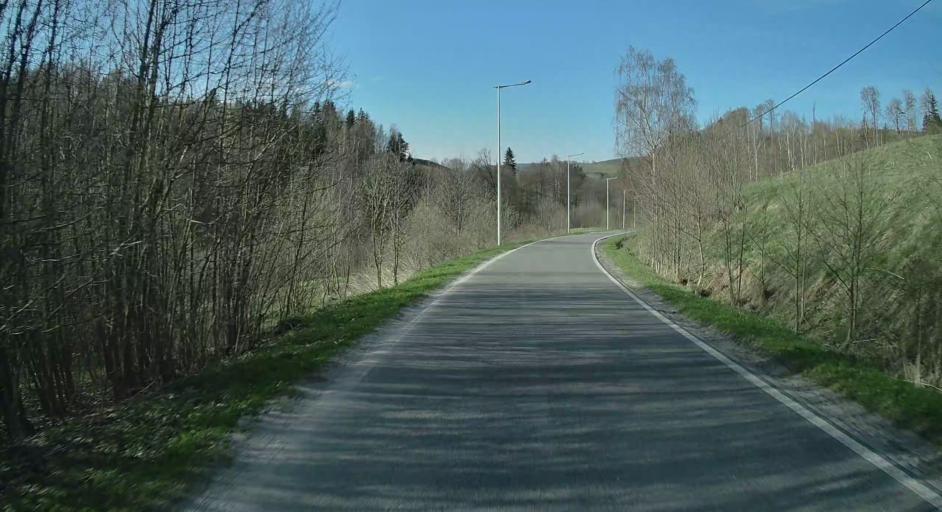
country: PL
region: Lower Silesian Voivodeship
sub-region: Powiat klodzki
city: Lewin Klodzki
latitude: 50.3895
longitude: 16.3002
